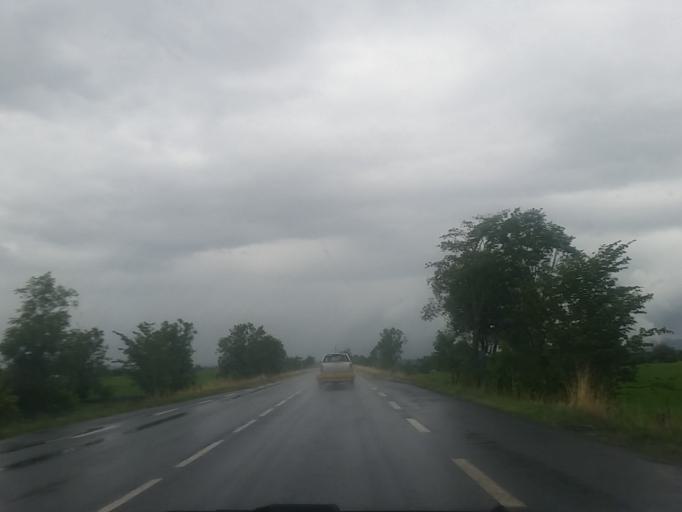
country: FR
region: Auvergne
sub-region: Departement du Cantal
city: Murat
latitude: 45.0909
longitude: 2.9263
